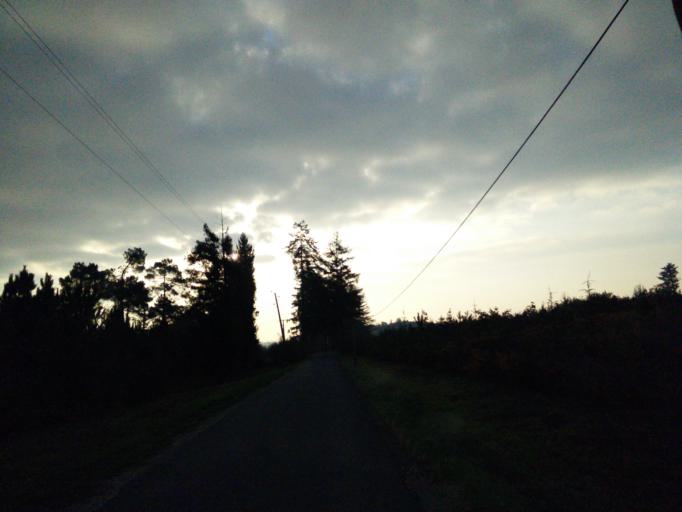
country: FR
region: Aquitaine
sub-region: Departement de la Dordogne
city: Rouffignac-Saint-Cernin-de-Reilhac
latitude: 45.0182
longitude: 0.9759
